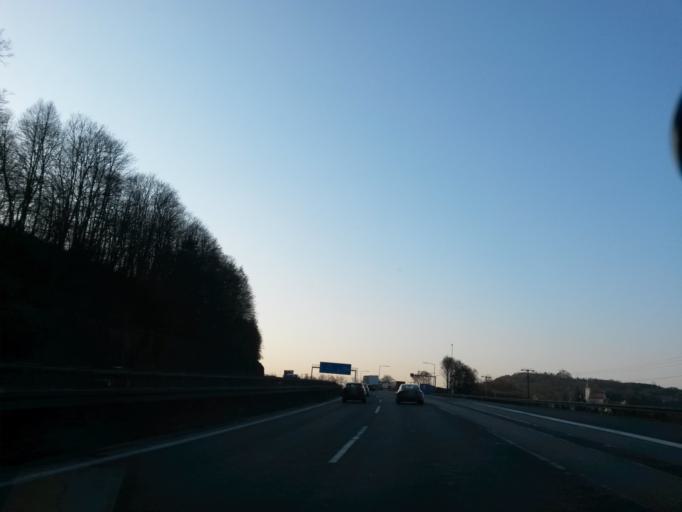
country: DE
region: Bavaria
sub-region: Regierungsbezirk Mittelfranken
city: Greding
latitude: 49.0392
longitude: 11.3571
